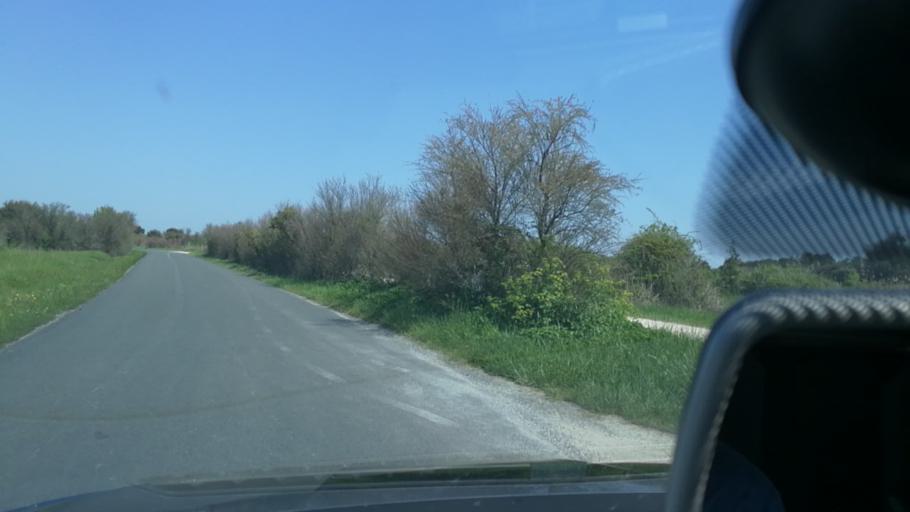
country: FR
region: Poitou-Charentes
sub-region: Departement de la Charente-Maritime
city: Saint-Trojan-les-Bains
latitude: 45.8636
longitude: -1.2285
